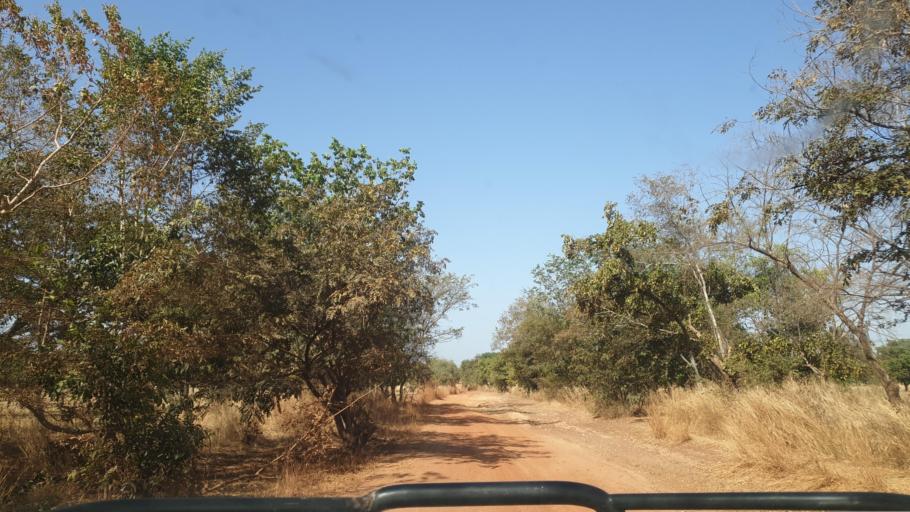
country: ML
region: Sikasso
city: Bougouni
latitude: 11.8212
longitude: -6.9672
